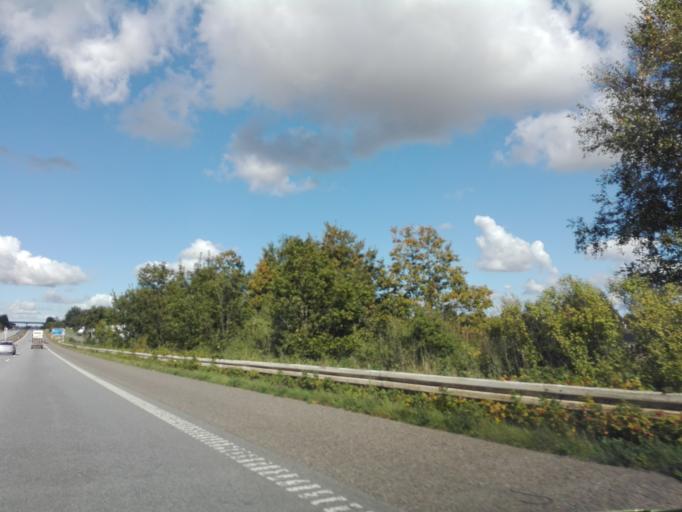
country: DK
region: Central Jutland
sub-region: Randers Kommune
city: Randers
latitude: 56.4790
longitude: 9.9814
